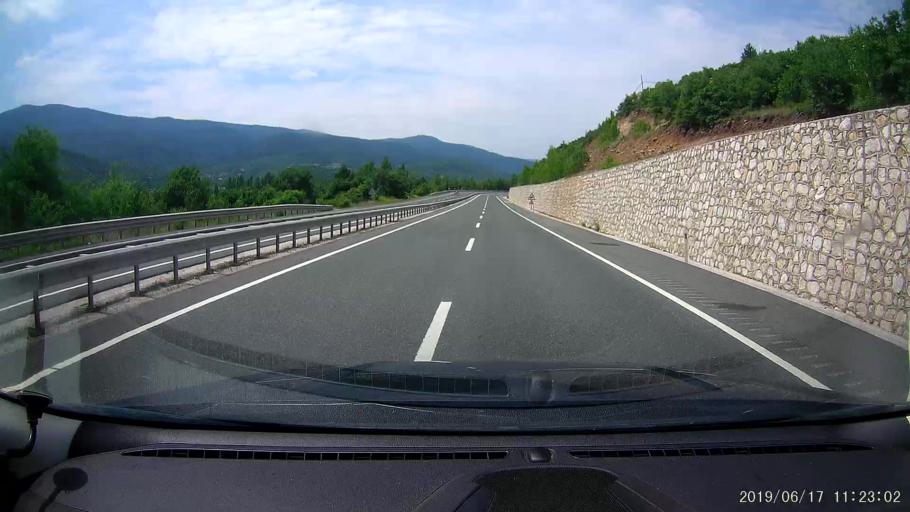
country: TR
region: Cankiri
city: Ilgaz
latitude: 40.8935
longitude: 33.7401
